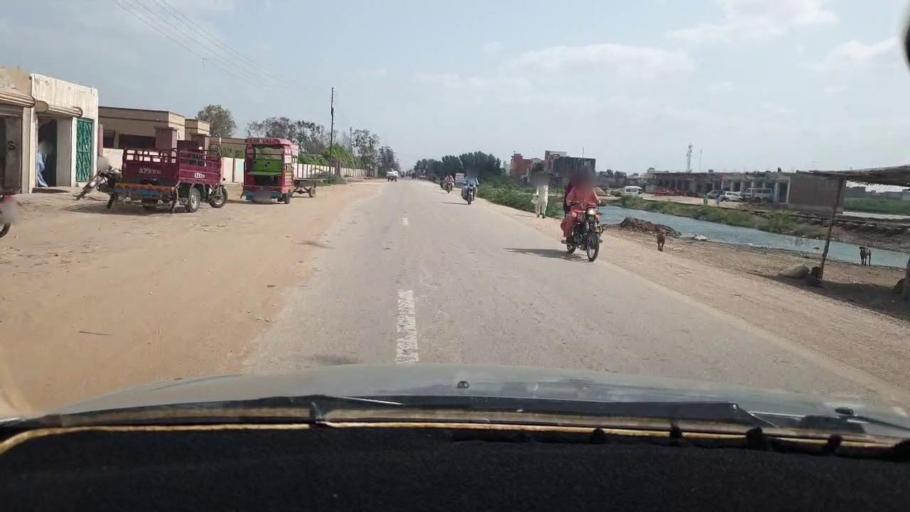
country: PK
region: Sindh
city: Naukot
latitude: 24.9746
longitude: 69.2956
